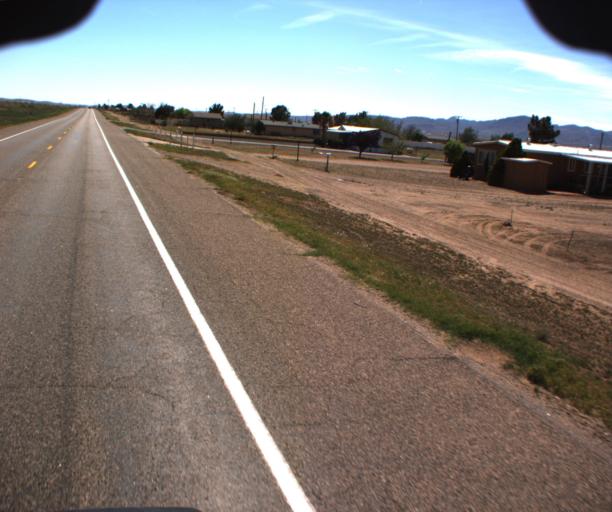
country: US
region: Arizona
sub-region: Mohave County
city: New Kingman-Butler
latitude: 35.2991
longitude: -113.9325
